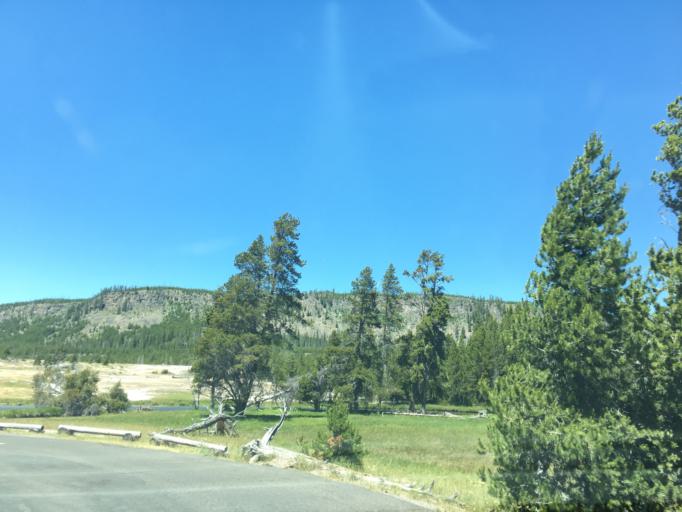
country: US
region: Montana
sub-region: Gallatin County
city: West Yellowstone
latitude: 44.4857
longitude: -110.8521
